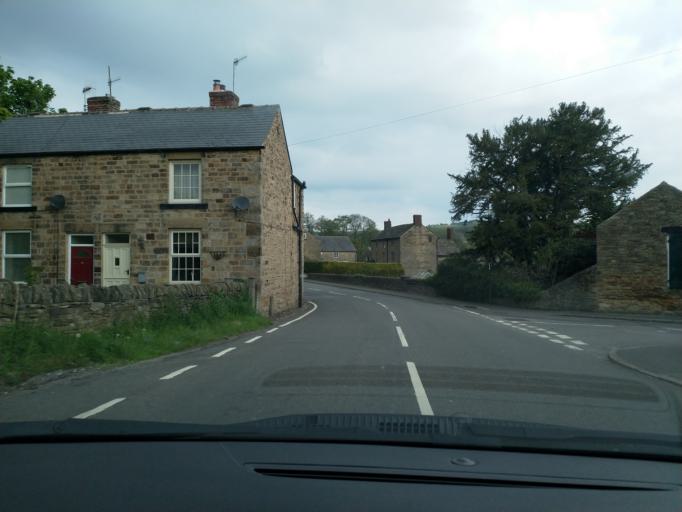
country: GB
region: England
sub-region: Derbyshire
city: Dronfield
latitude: 53.2765
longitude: -1.4974
